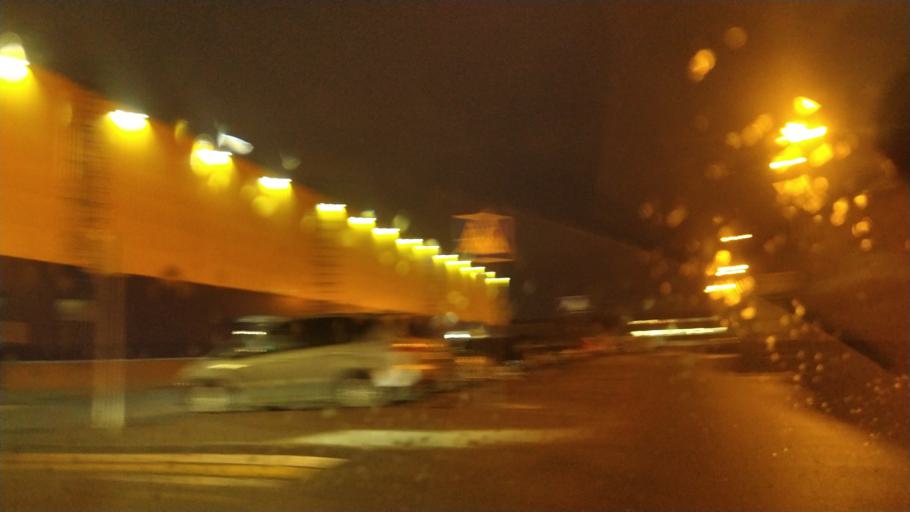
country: RU
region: Leningrad
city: Bugry
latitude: 60.0606
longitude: 30.3936
